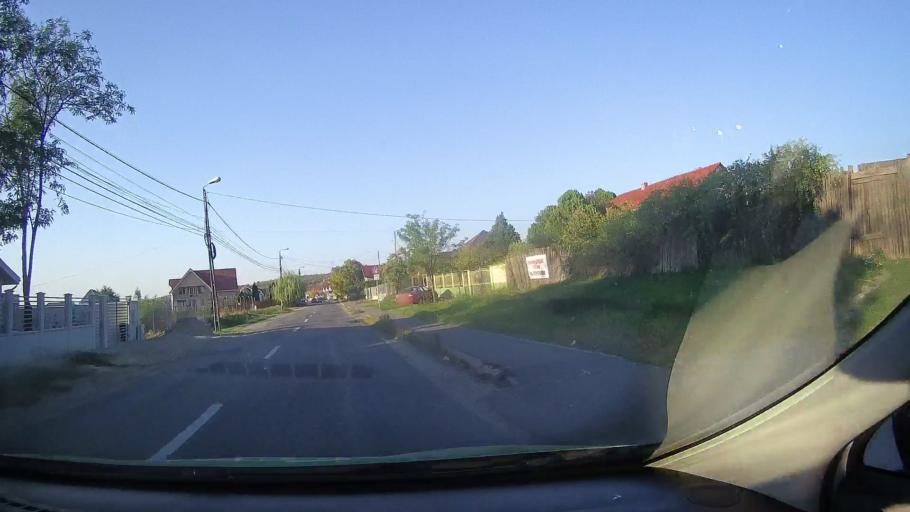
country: RO
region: Bihor
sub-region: Comuna Biharea
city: Oradea
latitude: 47.0897
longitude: 21.9264
